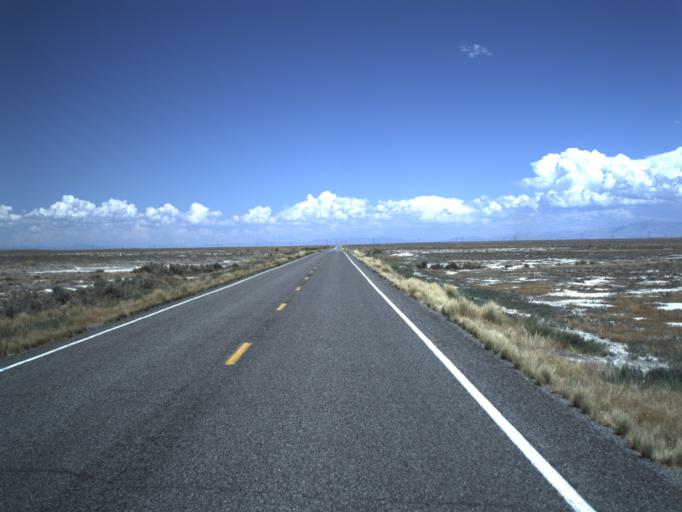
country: US
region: Utah
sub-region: Millard County
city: Delta
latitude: 39.2075
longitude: -112.9711
